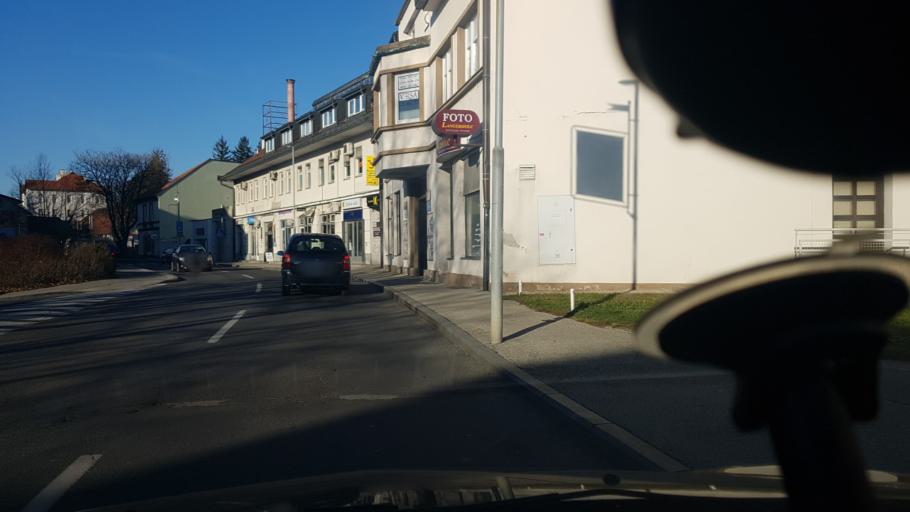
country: SI
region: Ptuj
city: Ptuj
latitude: 46.4206
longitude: 15.8740
